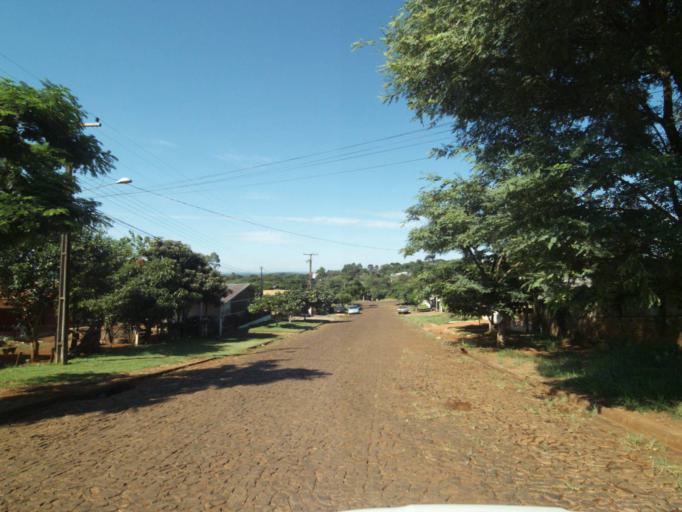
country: BR
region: Parana
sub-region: Laranjeiras Do Sul
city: Laranjeiras do Sul
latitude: -25.4940
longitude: -52.5265
